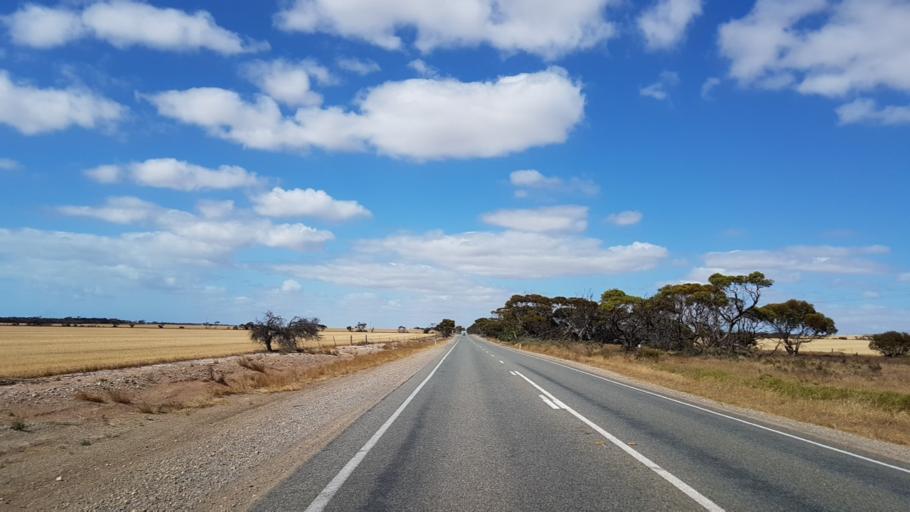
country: AU
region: South Australia
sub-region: Yorke Peninsula
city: Ardrossan
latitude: -34.2280
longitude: 138.0066
